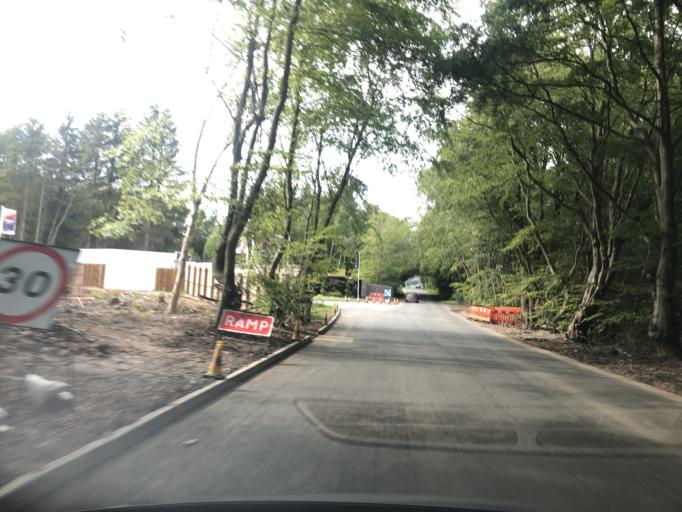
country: GB
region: Scotland
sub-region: Midlothian
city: Penicuik
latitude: 55.8458
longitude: -3.2265
